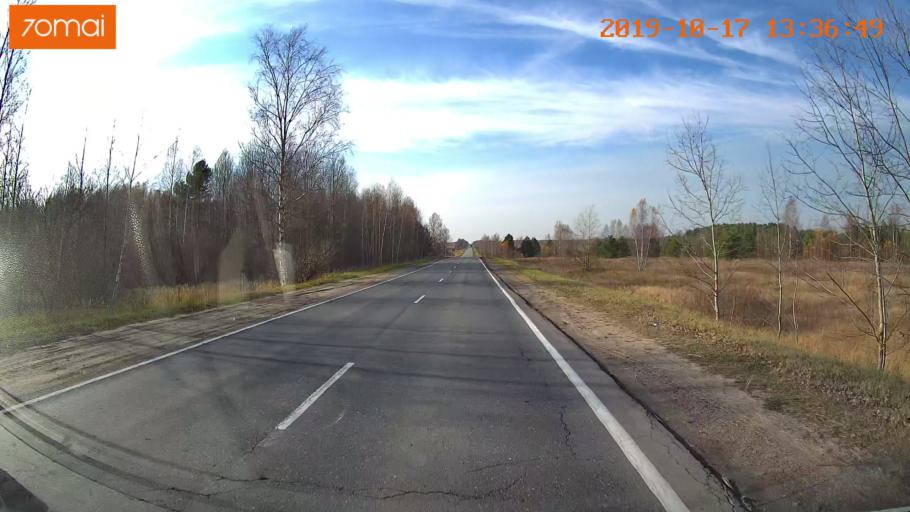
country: RU
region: Rjazan
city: Tuma
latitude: 55.1402
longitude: 40.6541
